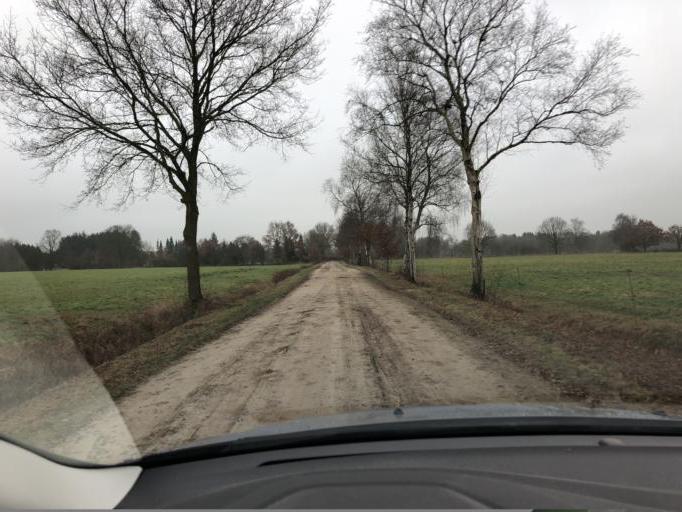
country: DE
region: Lower Saxony
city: Bad Zwischenahn
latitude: 53.1711
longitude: 8.0446
